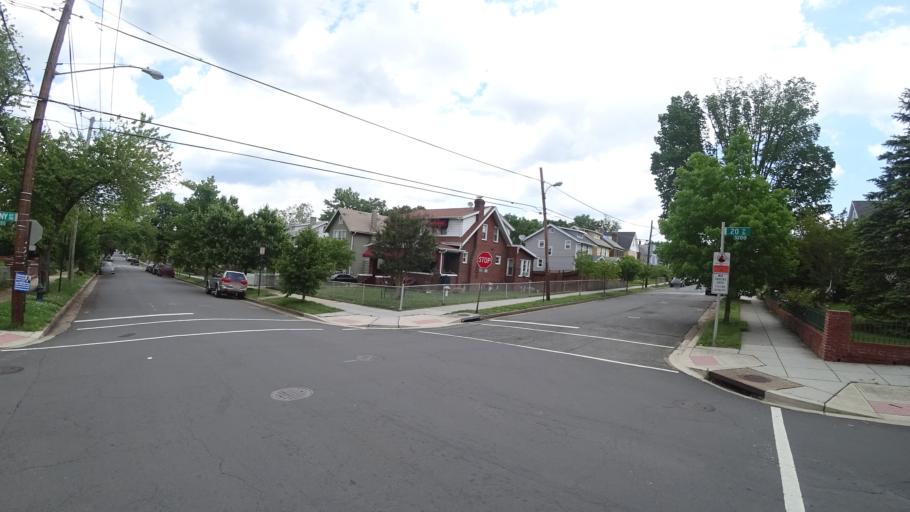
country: US
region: Maryland
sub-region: Prince George's County
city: Mount Rainier
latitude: 38.9311
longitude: -76.9763
